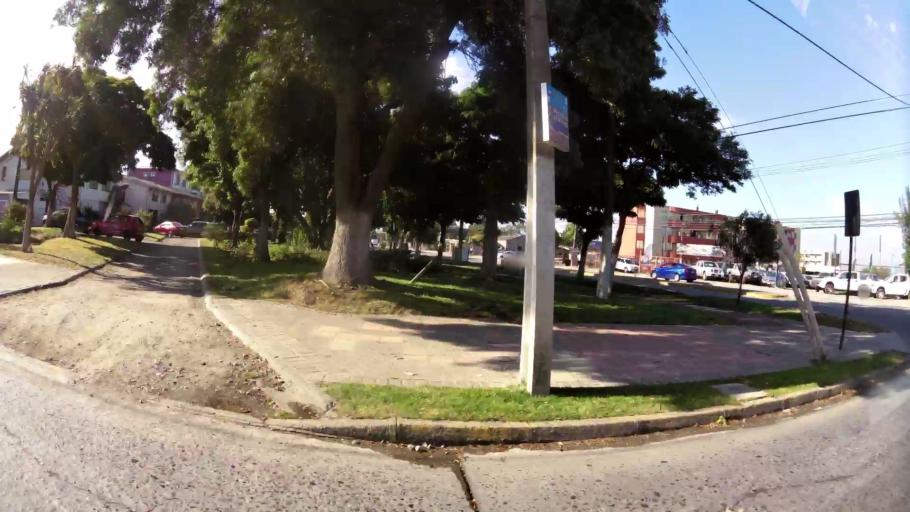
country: CL
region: Biobio
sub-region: Provincia de Concepcion
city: Concepcion
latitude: -36.7959
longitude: -73.0866
